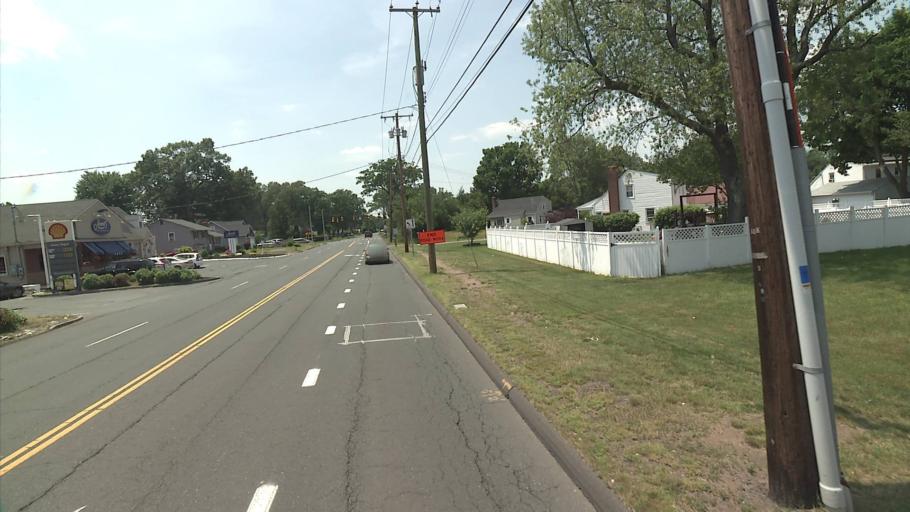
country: US
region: Connecticut
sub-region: Hartford County
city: East Hartford
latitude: 41.7658
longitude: -72.5785
